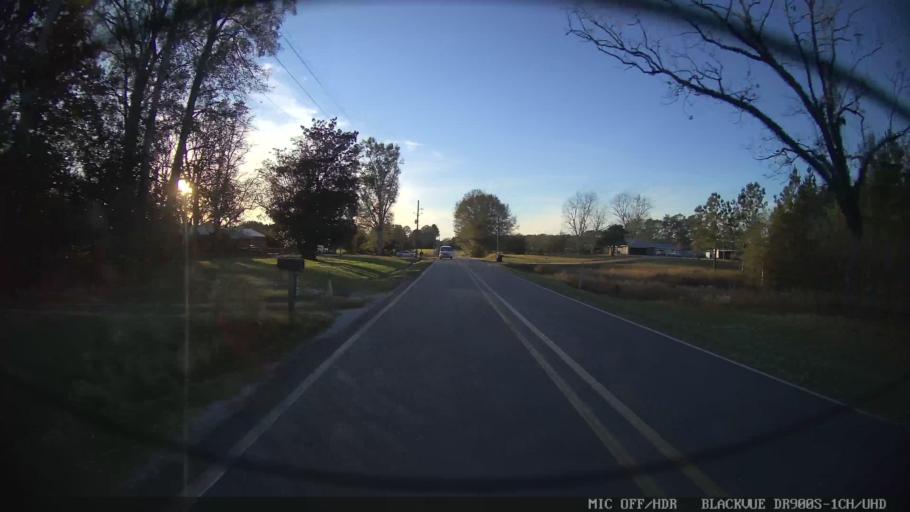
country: US
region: Mississippi
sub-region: Lamar County
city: Lumberton
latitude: 30.9975
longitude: -89.3977
